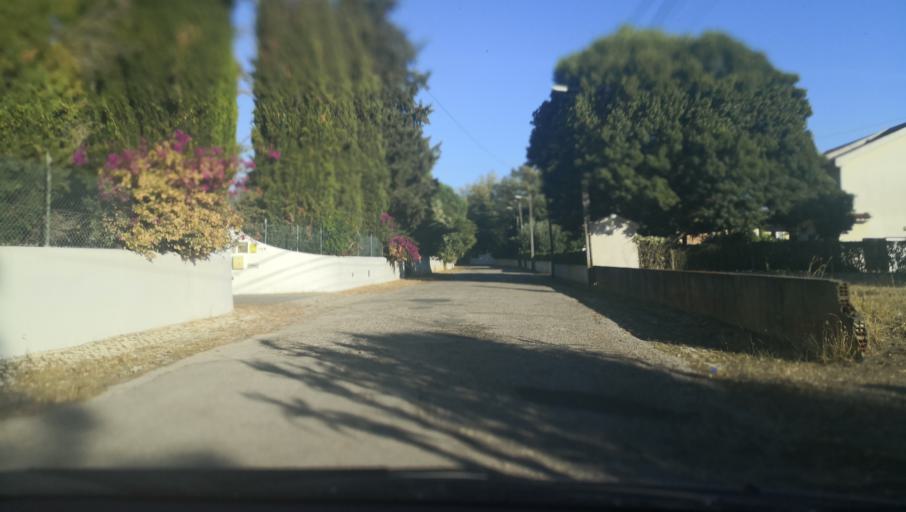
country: PT
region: Setubal
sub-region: Palmela
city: Palmela
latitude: 38.5526
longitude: -8.8892
